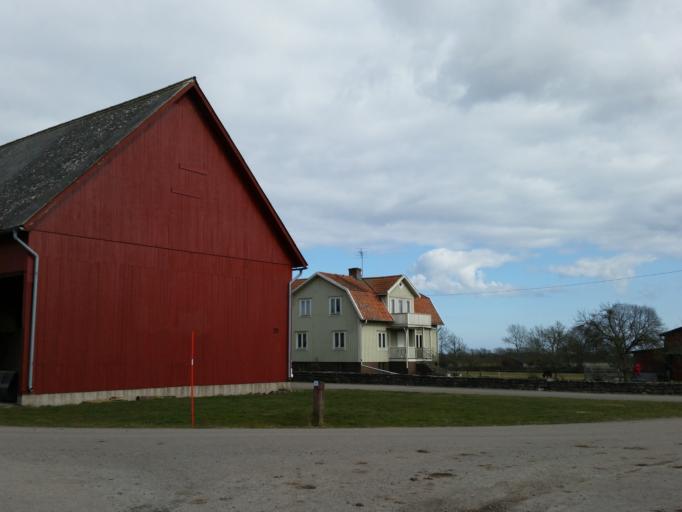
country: SE
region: Kalmar
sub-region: Morbylanga Kommun
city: Sodra Sandby
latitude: 56.6748
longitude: 16.6507
